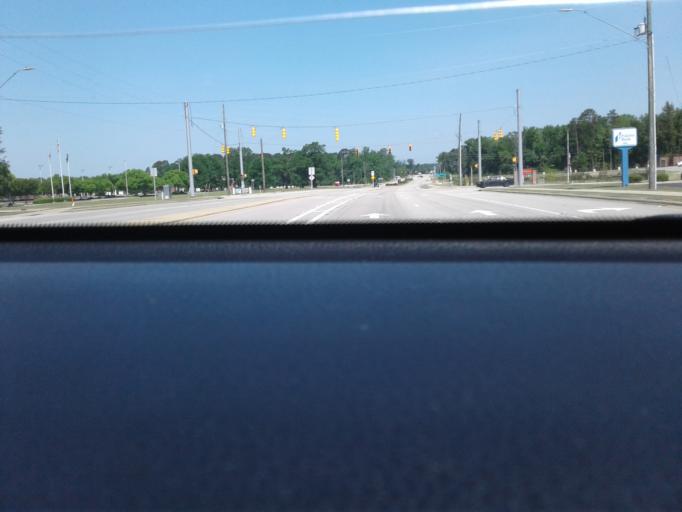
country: US
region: North Carolina
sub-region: Harnett County
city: Lillington
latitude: 35.4195
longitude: -78.8065
